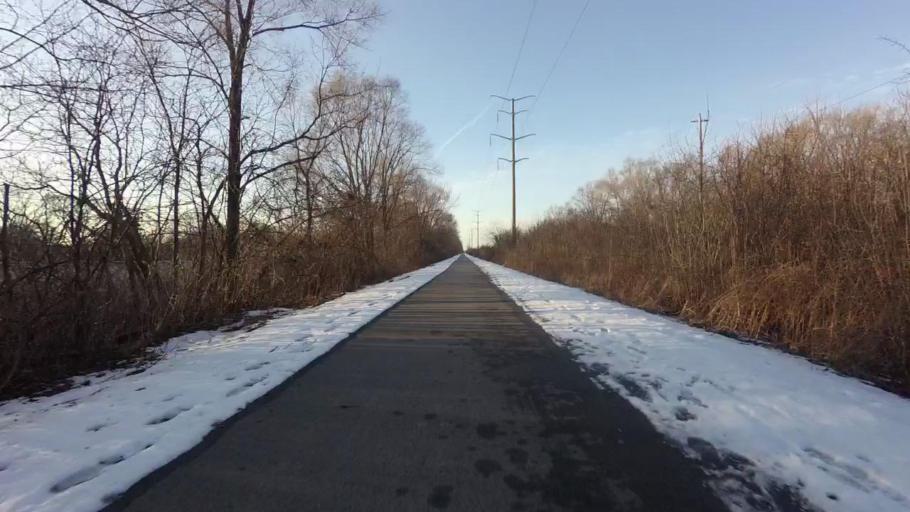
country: US
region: Wisconsin
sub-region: Milwaukee County
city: Glendale
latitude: 43.1205
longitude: -87.9338
